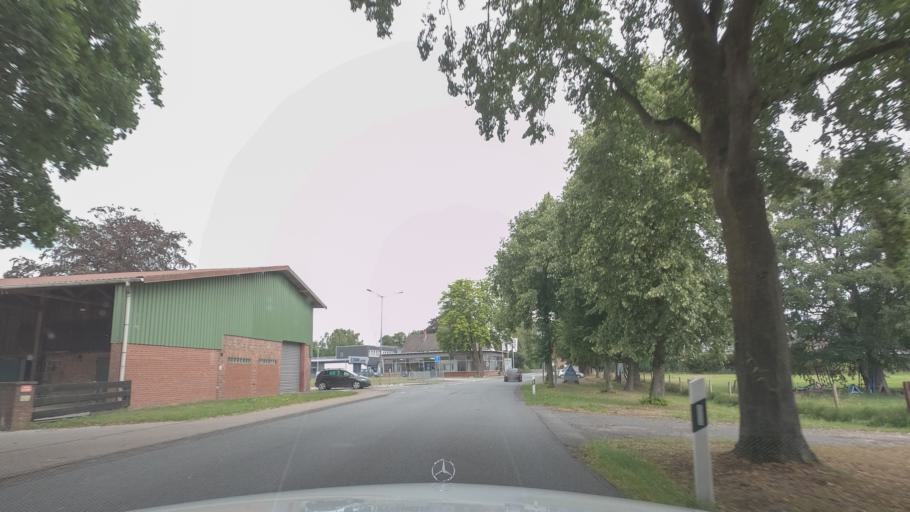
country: DE
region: Lower Saxony
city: Neuenkirchen
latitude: 53.2329
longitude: 8.5267
